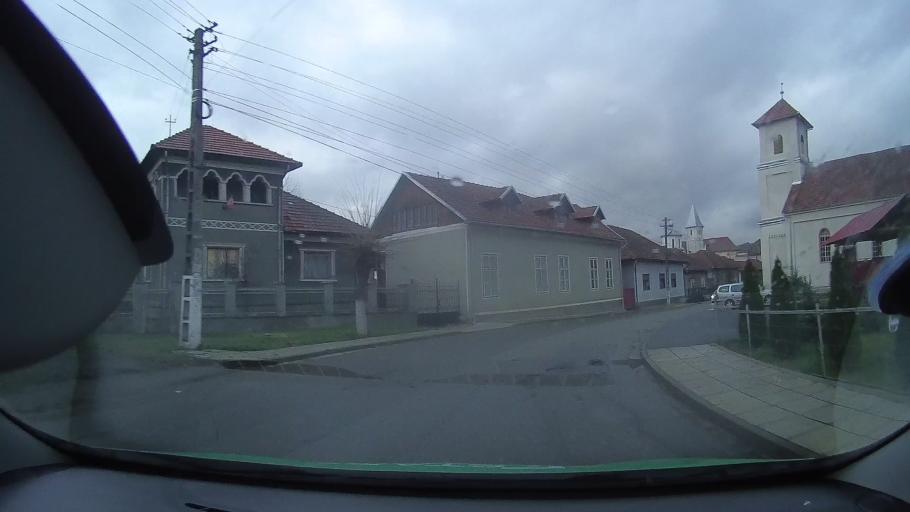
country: RO
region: Hunedoara
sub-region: Comuna Baia de Cris
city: Baia de Cris
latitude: 46.1743
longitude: 22.7154
